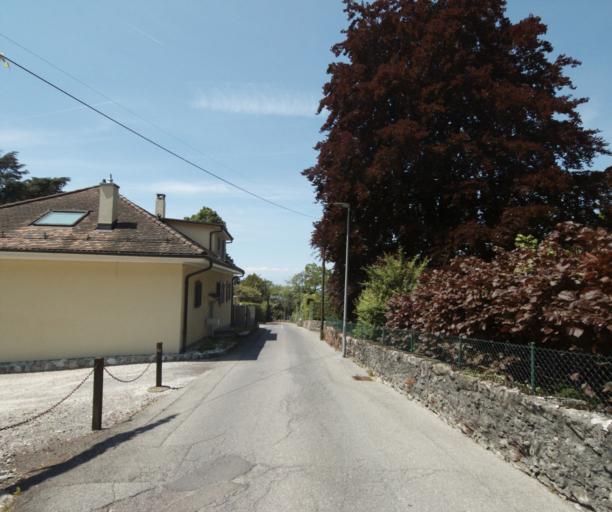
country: CH
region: Vaud
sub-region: Aigle District
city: Villeneuve
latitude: 46.4051
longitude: 6.9311
